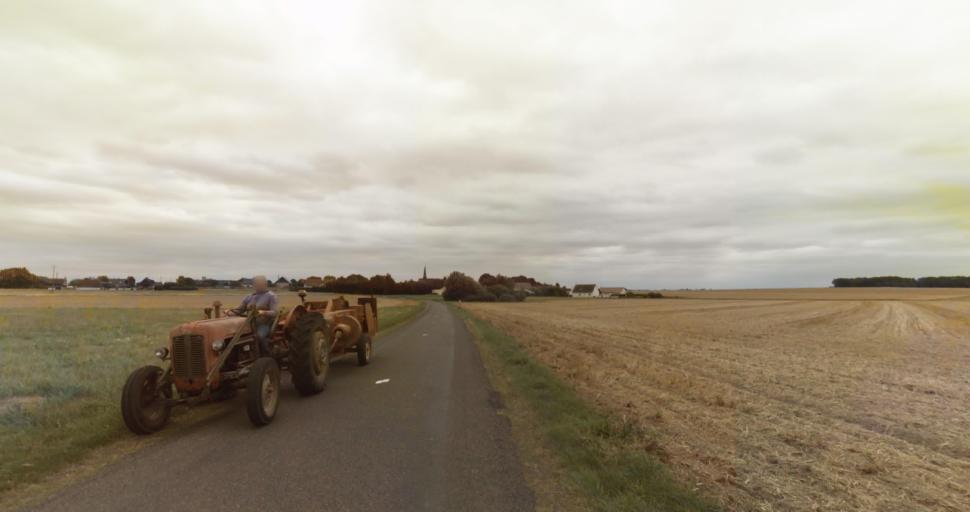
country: FR
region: Haute-Normandie
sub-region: Departement de l'Eure
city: Marcilly-sur-Eure
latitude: 48.9339
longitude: 1.2691
